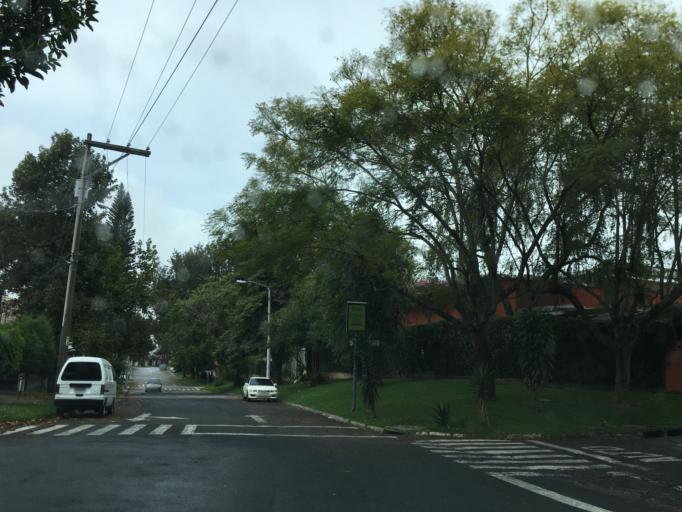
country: GT
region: Guatemala
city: Santa Catarina Pinula
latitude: 14.5891
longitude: -90.4954
